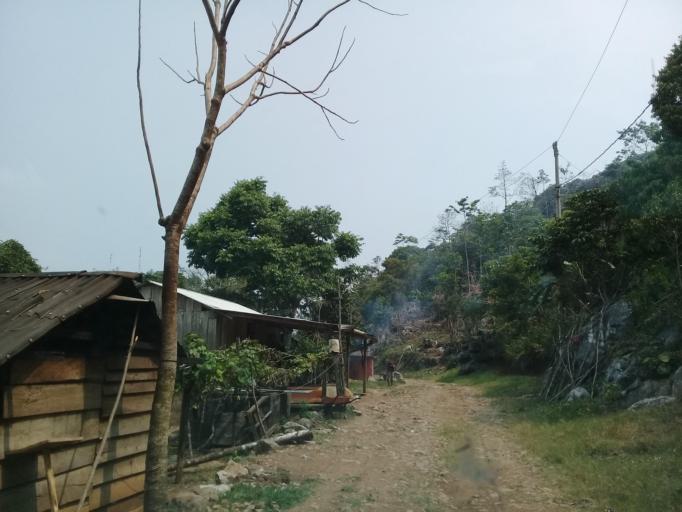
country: MX
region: Veracruz
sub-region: Tezonapa
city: Laguna Chica (Pueblo Nuevo)
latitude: 18.5899
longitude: -96.7470
